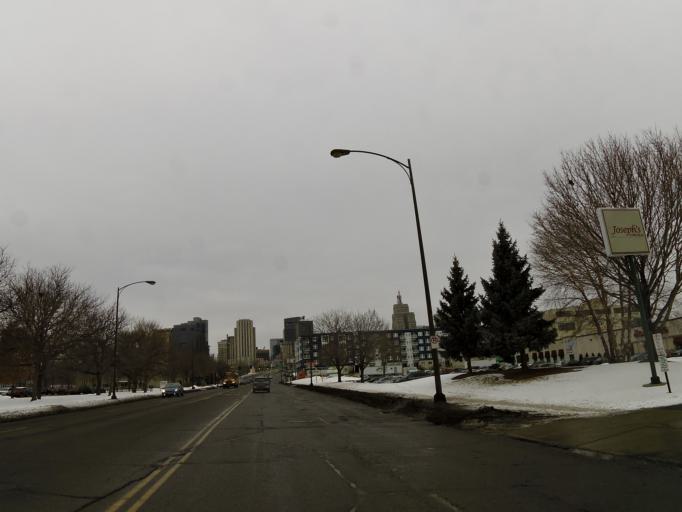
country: US
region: Minnesota
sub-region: Ramsey County
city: Saint Paul
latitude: 44.9379
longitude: -93.0882
